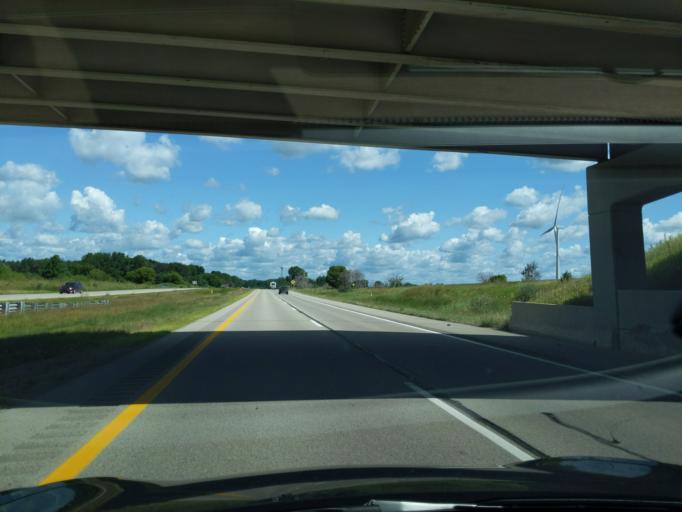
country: US
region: Michigan
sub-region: Isabella County
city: Shepherd
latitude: 43.5241
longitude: -84.6766
